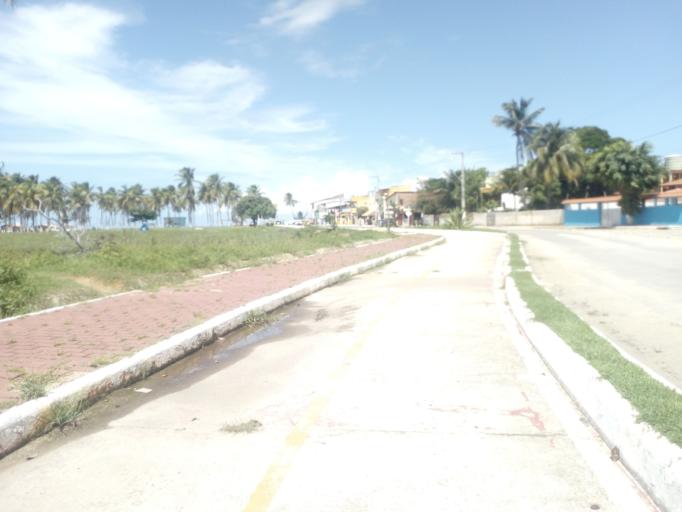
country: BR
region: Pernambuco
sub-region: Sirinhaem
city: Sirinhaem
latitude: -8.5251
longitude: -35.0096
